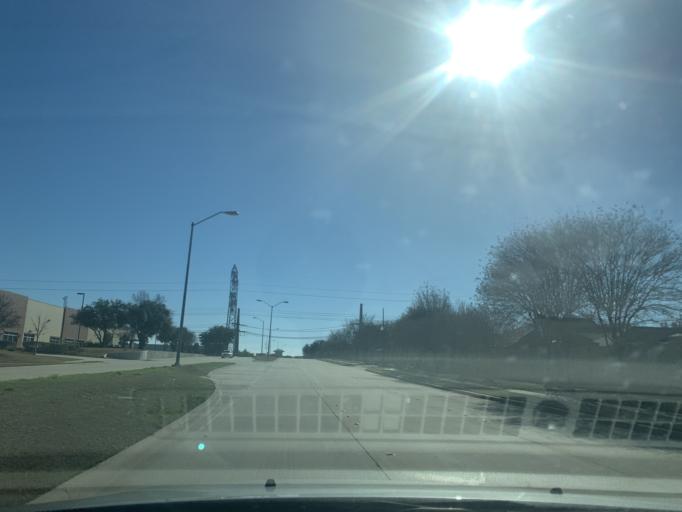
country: US
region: Texas
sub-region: Denton County
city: The Colony
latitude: 33.0609
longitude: -96.8329
